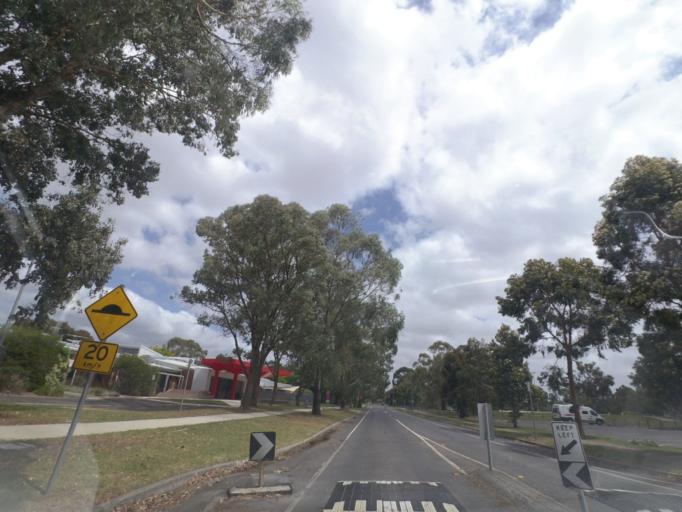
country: AU
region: Victoria
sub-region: Maroondah
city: Croydon South
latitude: -37.8011
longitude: 145.2850
